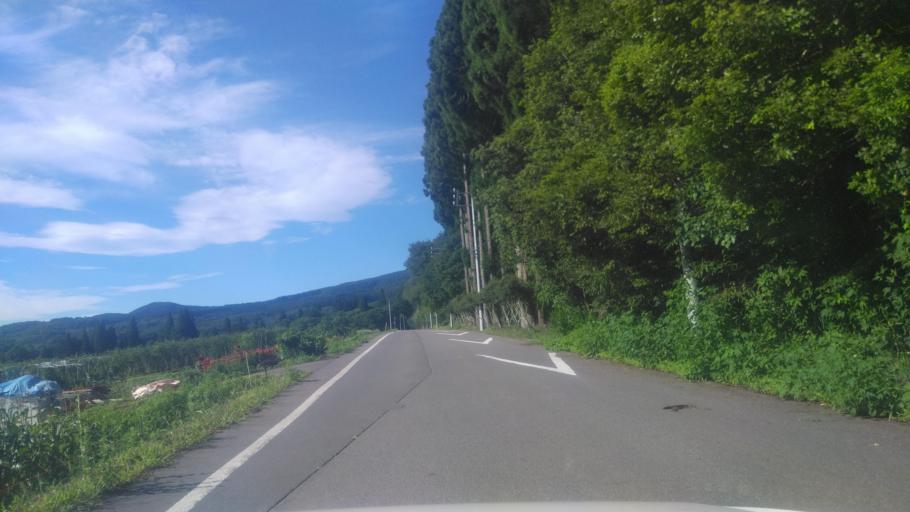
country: JP
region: Nagano
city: Nagano-shi
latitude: 36.7857
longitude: 138.1787
